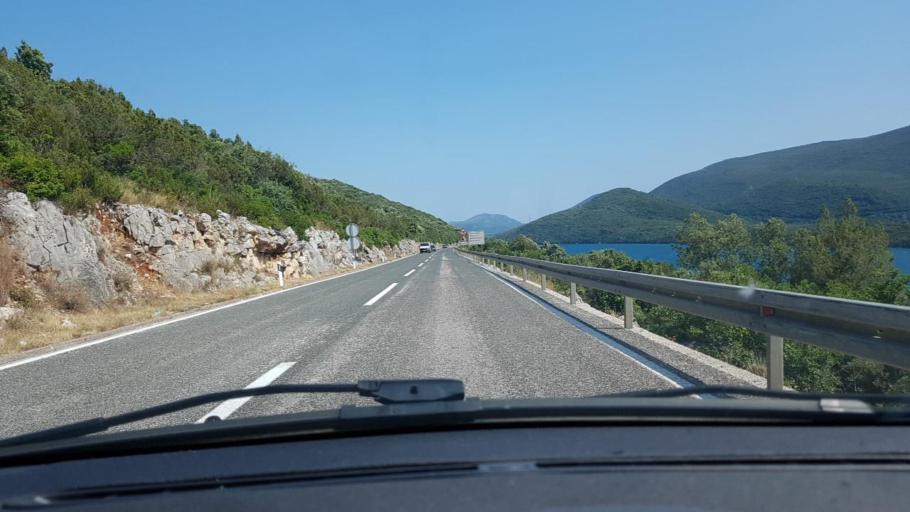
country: BA
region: Federation of Bosnia and Herzegovina
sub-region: Hercegovacko-Bosanski Kanton
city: Neum
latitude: 42.8867
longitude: 17.6546
